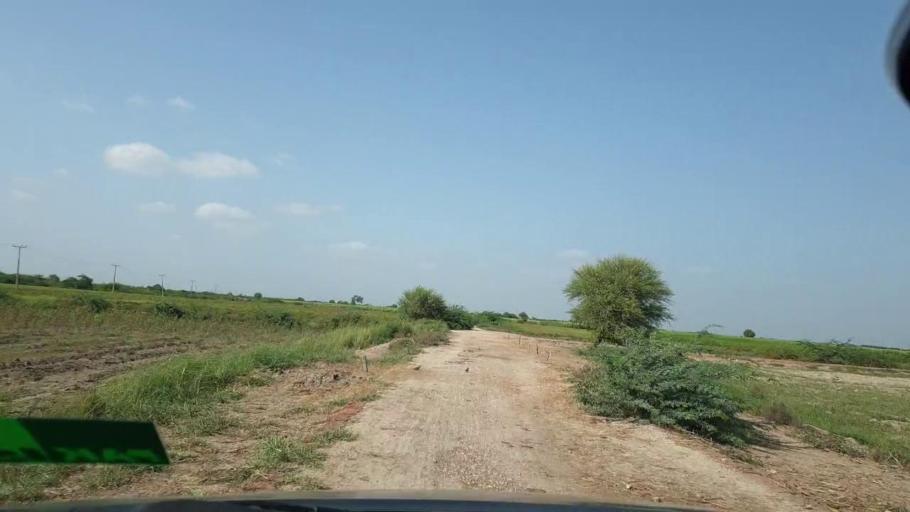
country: PK
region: Sindh
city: Tando Bago
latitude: 24.6858
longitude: 69.2055
